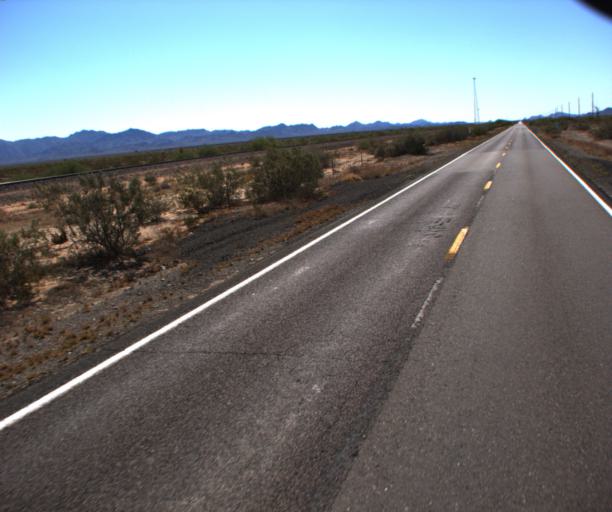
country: US
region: Arizona
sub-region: La Paz County
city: Salome
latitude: 33.8440
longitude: -113.8946
